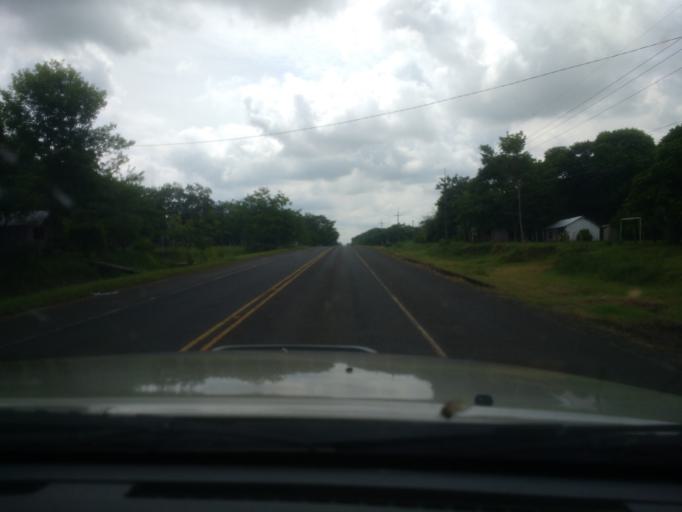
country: PY
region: San Pedro
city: Puerto Rosario
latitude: -24.4253
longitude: -57.0807
